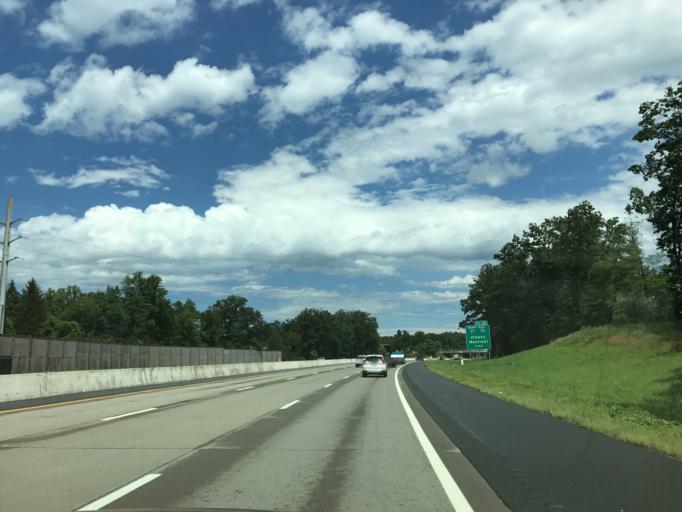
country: US
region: New York
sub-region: Albany County
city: McKownville
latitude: 42.6786
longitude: -73.8454
